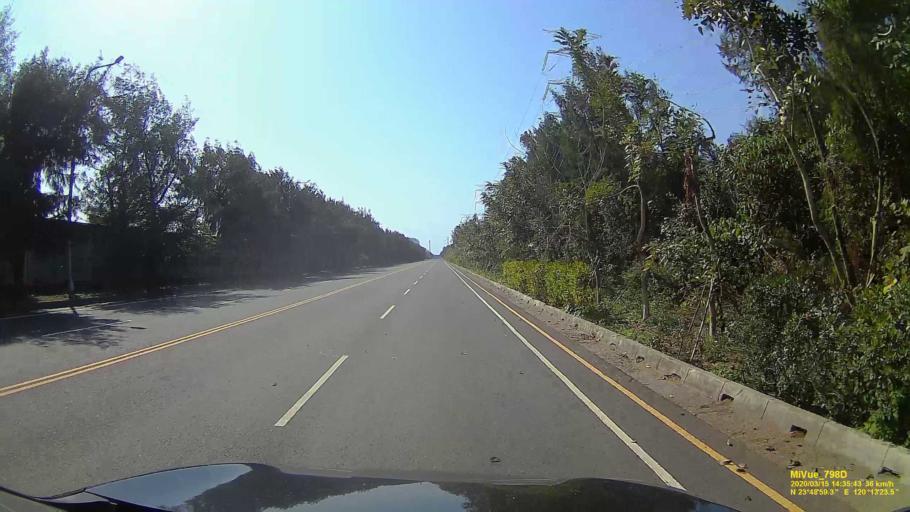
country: TW
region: Taiwan
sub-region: Yunlin
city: Douliu
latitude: 23.8165
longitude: 120.2230
